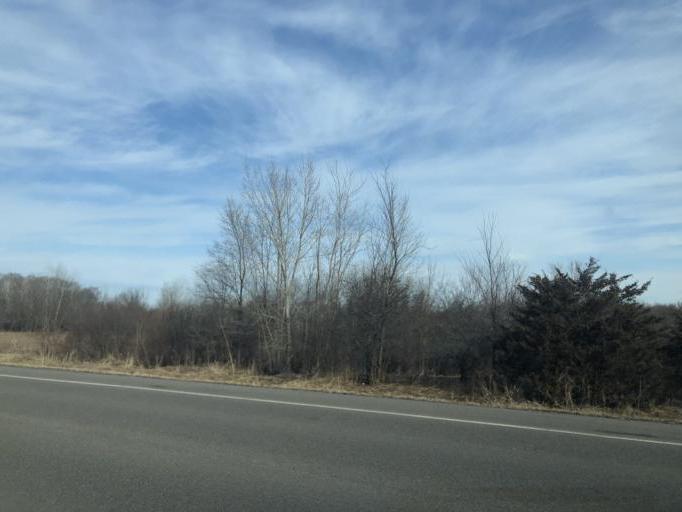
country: US
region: Minnesota
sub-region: Sherburne County
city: Becker
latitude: 45.3936
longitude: -93.8588
